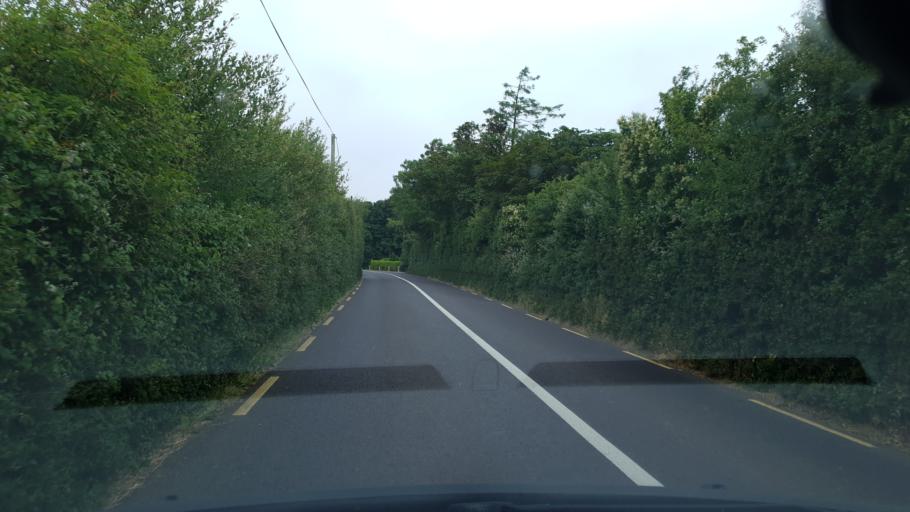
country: IE
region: Munster
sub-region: Ciarrai
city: Tralee
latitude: 52.1606
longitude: -9.6865
